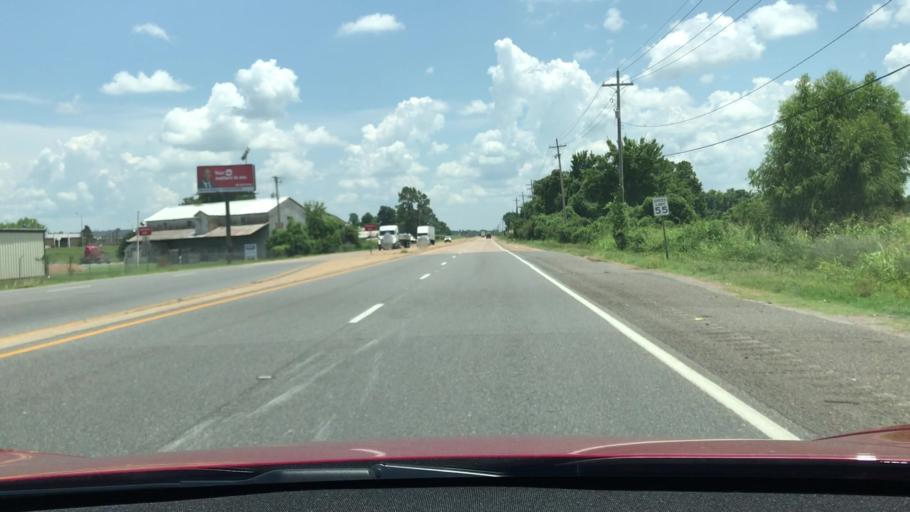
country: US
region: Louisiana
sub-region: Bossier Parish
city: Bossier City
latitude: 32.4006
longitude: -93.6932
